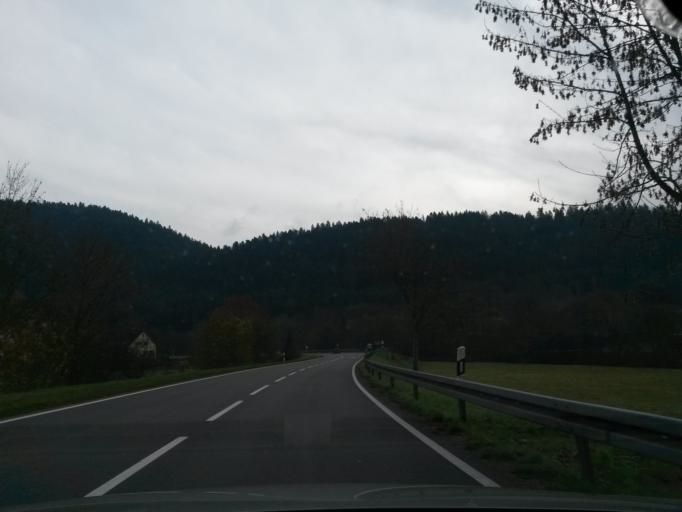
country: DE
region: Baden-Wuerttemberg
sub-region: Freiburg Region
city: Schenkenzell
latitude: 48.3014
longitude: 8.3633
